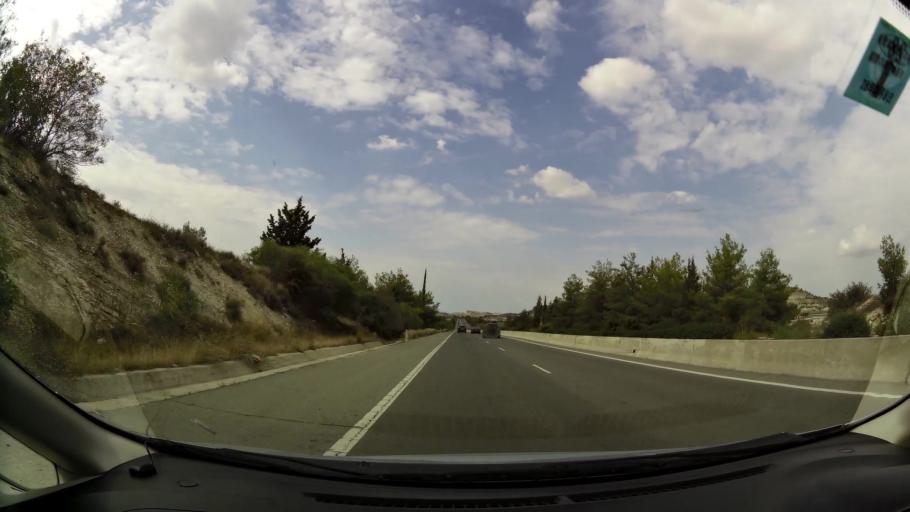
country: CY
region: Lefkosia
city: Dali
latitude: 34.9984
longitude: 33.4219
